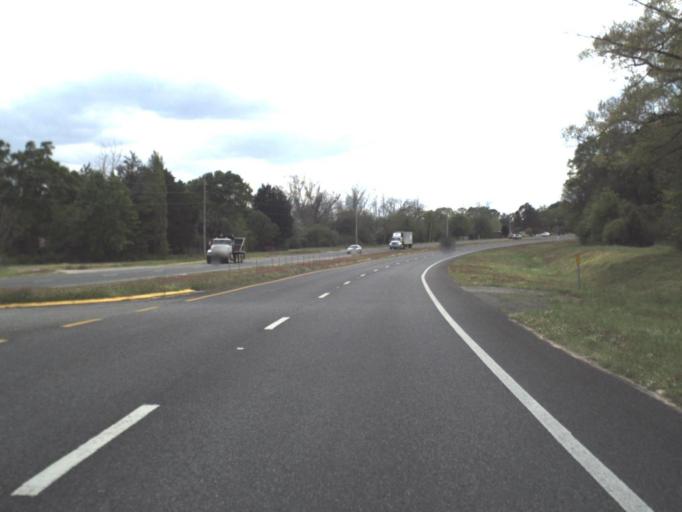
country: US
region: Florida
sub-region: Okaloosa County
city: Crestview
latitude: 30.8119
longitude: -86.5414
